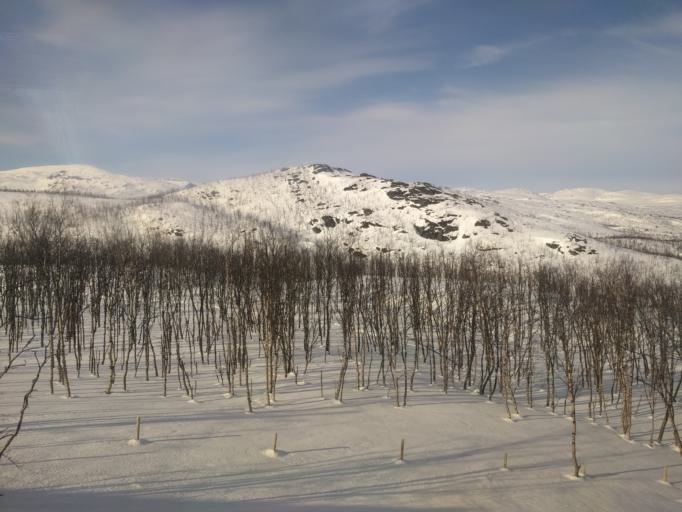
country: NO
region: Troms
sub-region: Bardu
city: Setermoen
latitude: 68.4254
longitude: 18.4340
